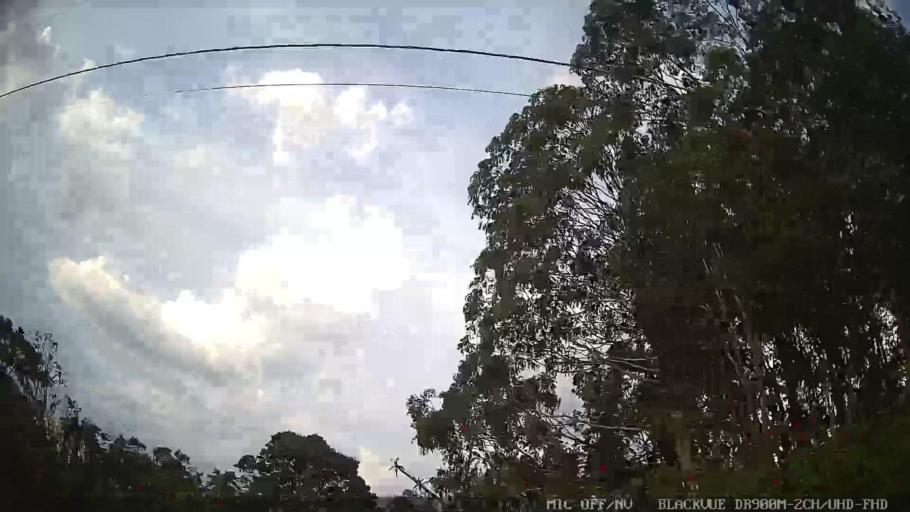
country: BR
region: Sao Paulo
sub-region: Braganca Paulista
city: Braganca Paulista
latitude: -22.9197
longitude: -46.5367
